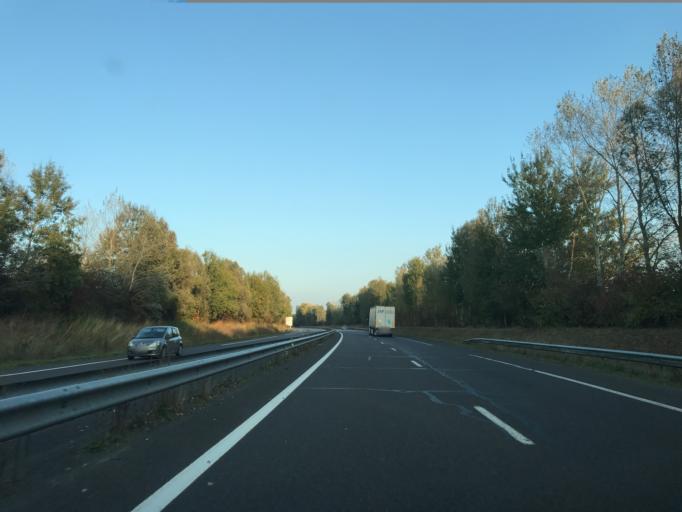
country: FR
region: Pays de la Loire
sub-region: Departement de la Sarthe
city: Mamers
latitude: 48.5064
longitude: 0.3735
